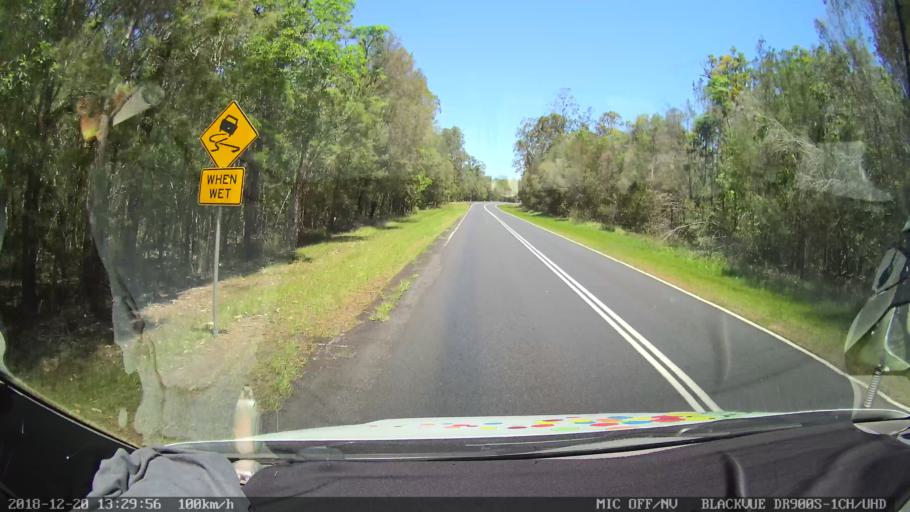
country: AU
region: New South Wales
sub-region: Clarence Valley
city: Gordon
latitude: -29.1964
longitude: 152.9917
